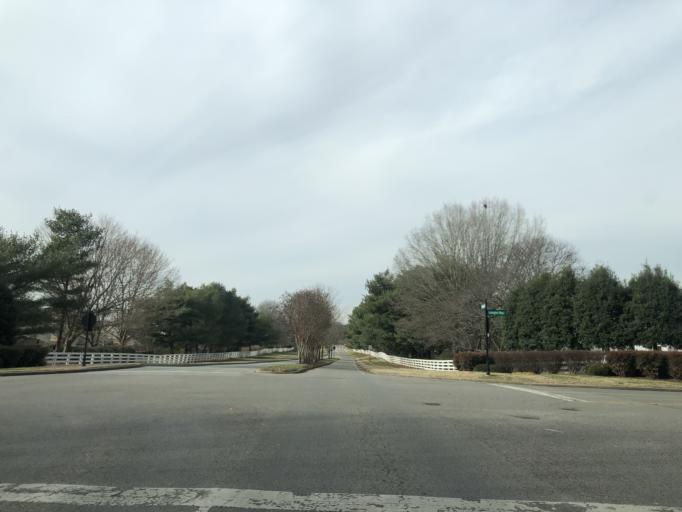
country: US
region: Tennessee
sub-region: Williamson County
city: Franklin
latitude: 35.9654
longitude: -86.8937
